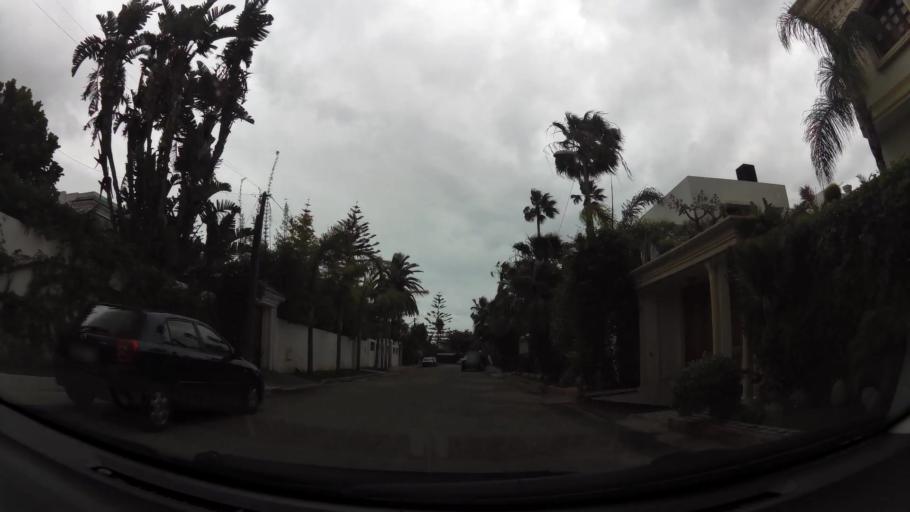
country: MA
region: Grand Casablanca
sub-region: Casablanca
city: Casablanca
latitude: 33.5788
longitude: -7.6648
